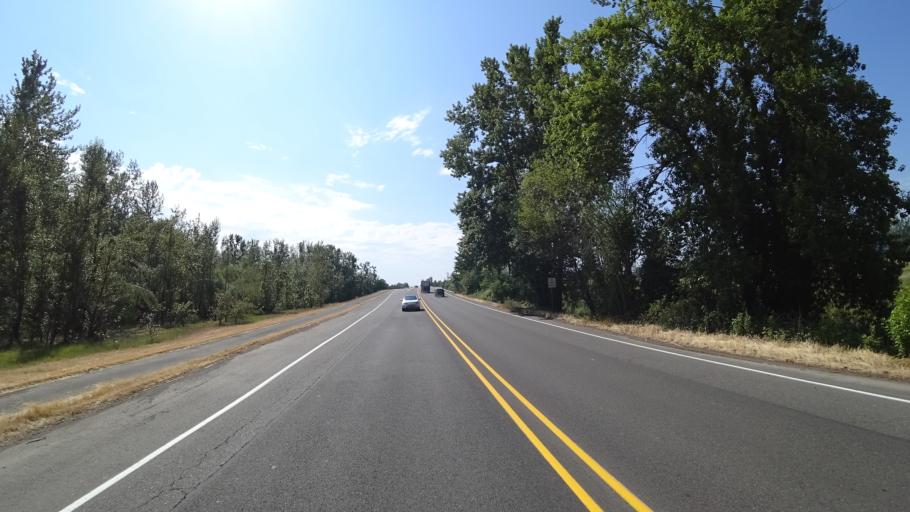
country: US
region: Oregon
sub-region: Multnomah County
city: Fairview
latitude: 45.5564
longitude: -122.4302
